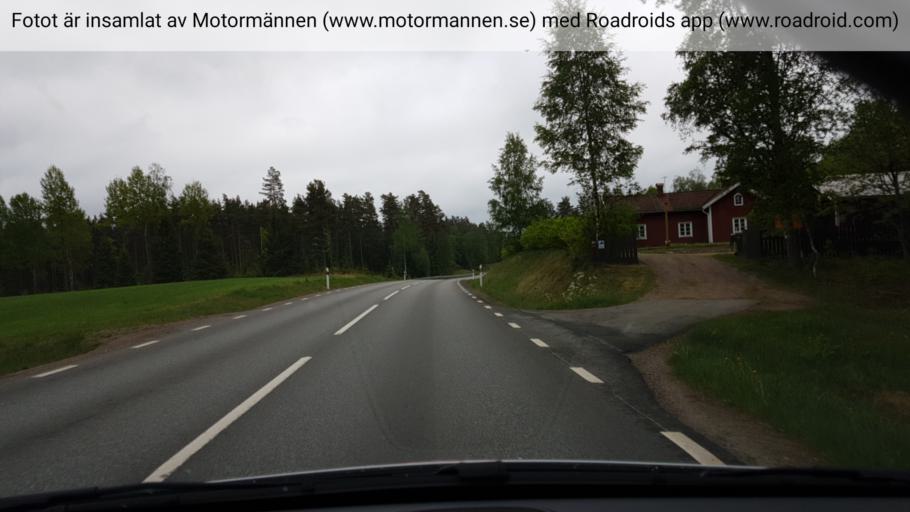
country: SE
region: Joenkoeping
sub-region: Mullsjo Kommun
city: Mullsjoe
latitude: 57.8690
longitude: 13.8564
